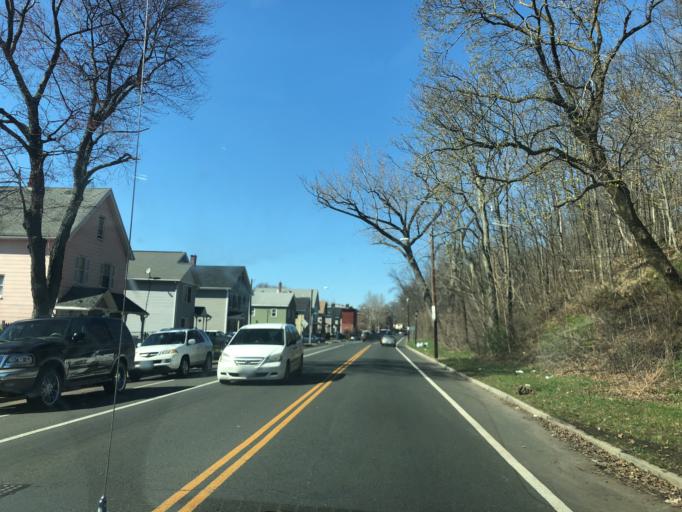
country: US
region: Connecticut
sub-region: Hartford County
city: Hartford
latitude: 41.7498
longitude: -72.6938
